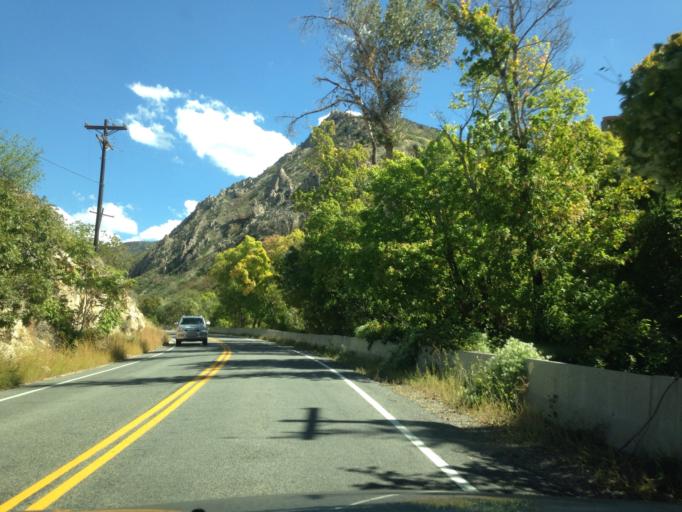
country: US
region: Utah
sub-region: Salt Lake County
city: Mount Olympus
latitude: 40.6891
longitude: -111.7875
